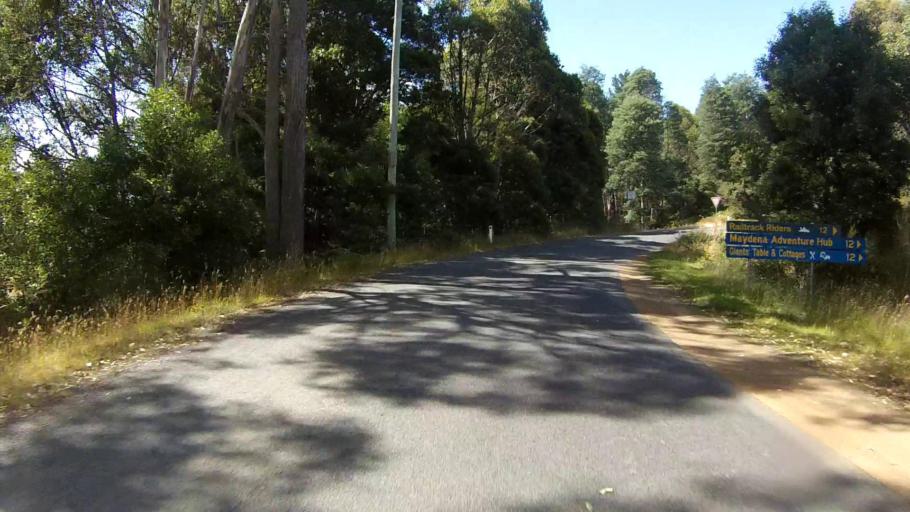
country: AU
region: Tasmania
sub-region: Derwent Valley
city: New Norfolk
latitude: -42.6847
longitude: 146.7219
